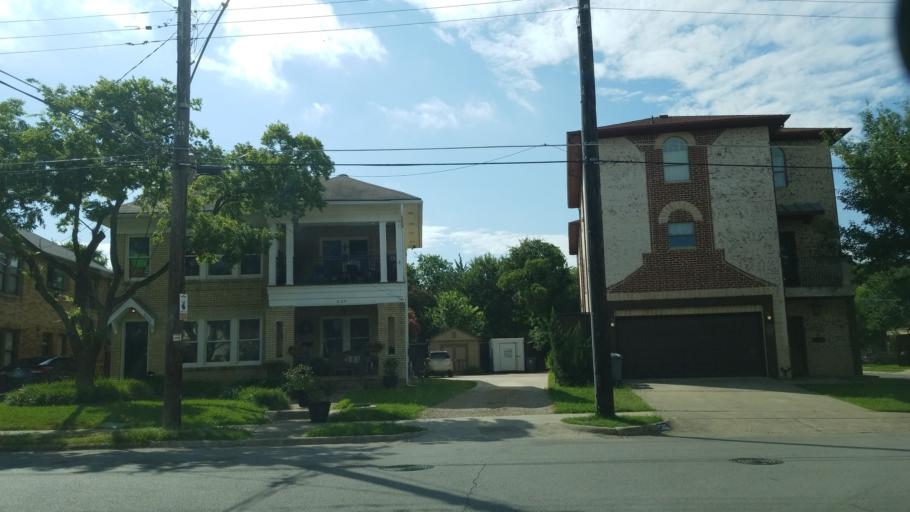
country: US
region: Texas
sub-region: Dallas County
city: Highland Park
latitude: 32.8160
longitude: -96.7833
